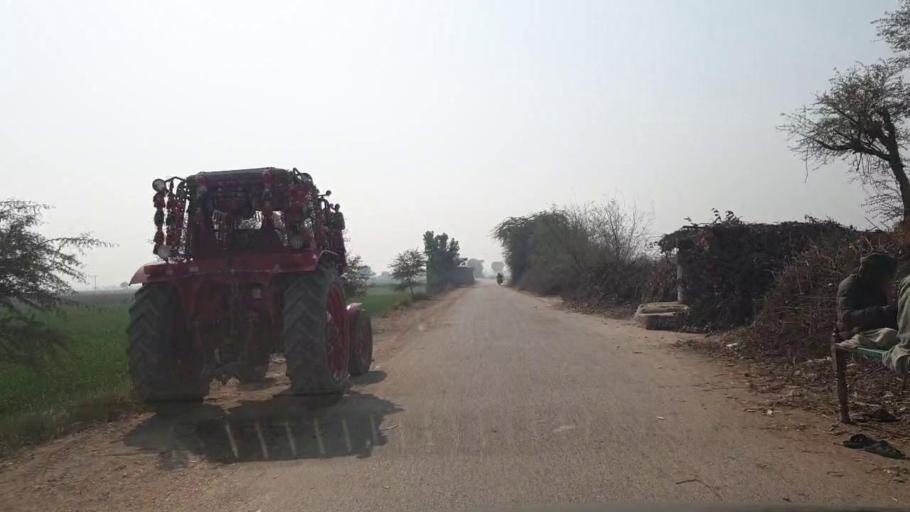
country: PK
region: Sindh
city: Hala
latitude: 25.8781
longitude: 68.4342
